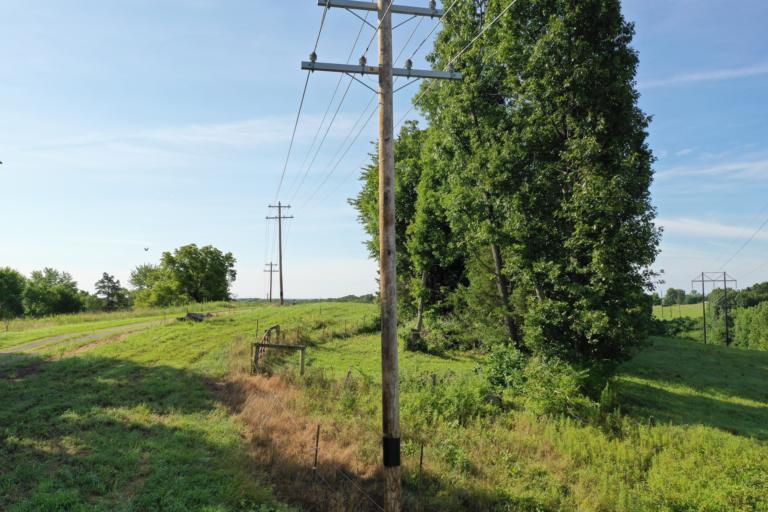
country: US
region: Missouri
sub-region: Callaway County
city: Holts Summit
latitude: 38.5363
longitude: -92.0525
